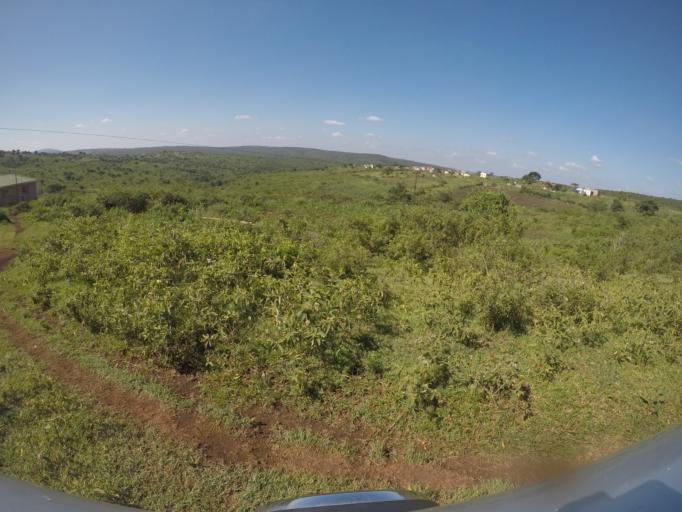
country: ZA
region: KwaZulu-Natal
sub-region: uThungulu District Municipality
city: Empangeni
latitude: -28.5606
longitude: 31.7015
